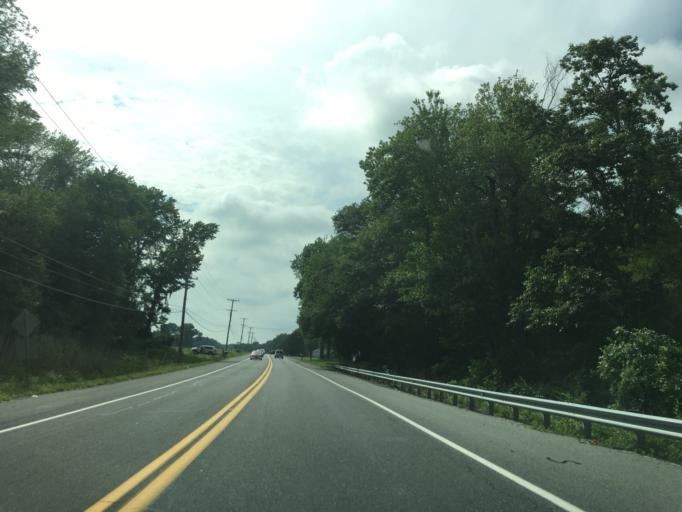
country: US
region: Delaware
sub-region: Sussex County
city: Long Neck
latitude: 38.5550
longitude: -75.1549
